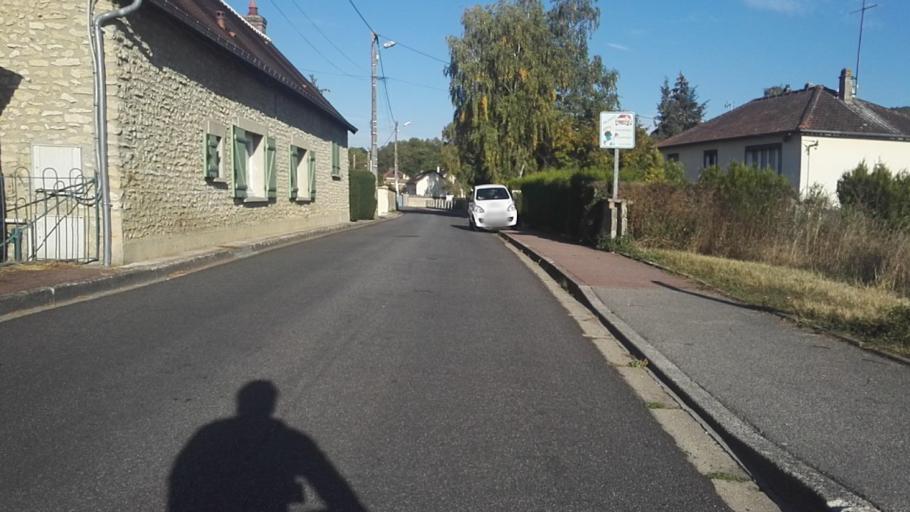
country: FR
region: Haute-Normandie
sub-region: Departement de l'Eure
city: Menilles
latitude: 49.0347
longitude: 1.3612
